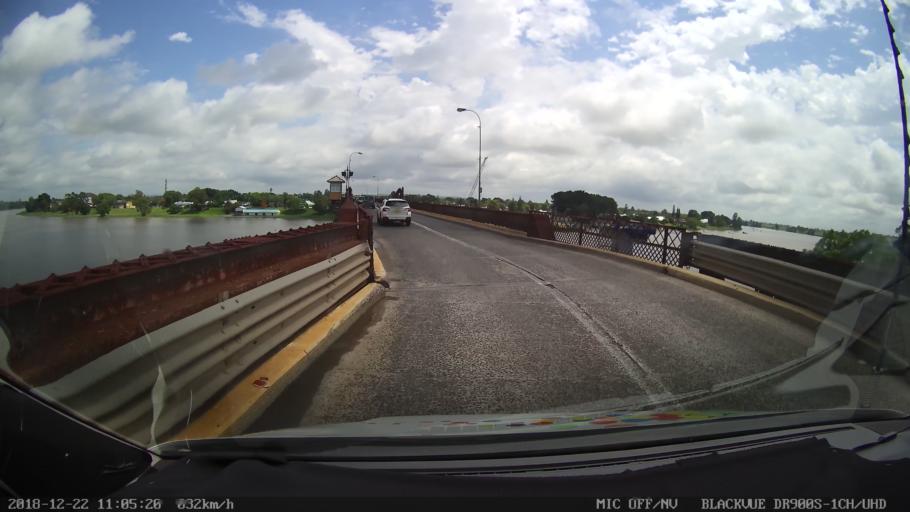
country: AU
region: New South Wales
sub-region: Clarence Valley
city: Grafton
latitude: -29.6998
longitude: 152.9425
